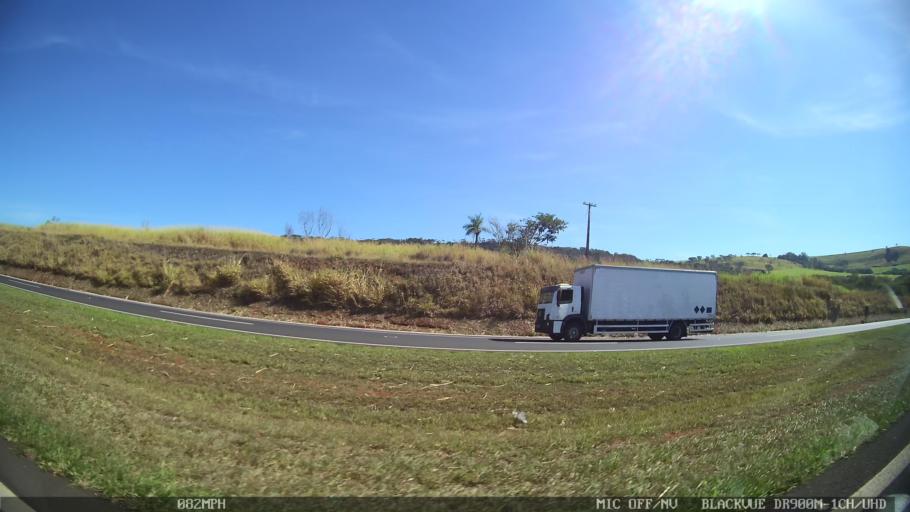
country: BR
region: Sao Paulo
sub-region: Sao Simao
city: Sao Simao
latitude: -21.4910
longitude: -47.6412
